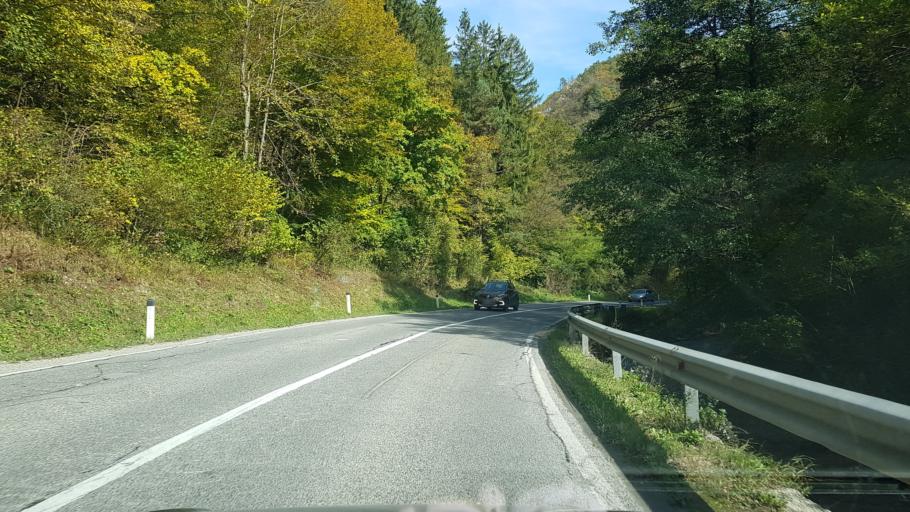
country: SI
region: Velenje
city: Velenje
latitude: 46.3868
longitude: 15.1616
